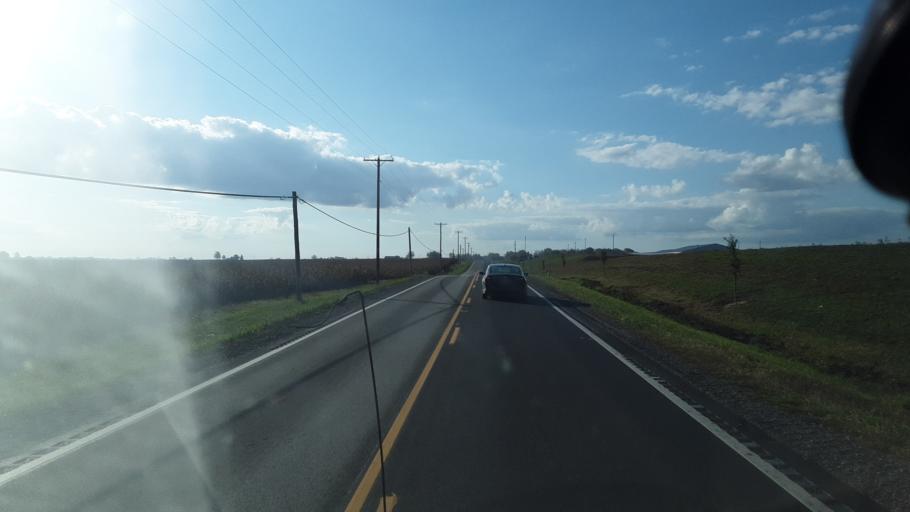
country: US
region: Ohio
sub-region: Fayette County
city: Jeffersonville
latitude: 39.6262
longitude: -83.5300
